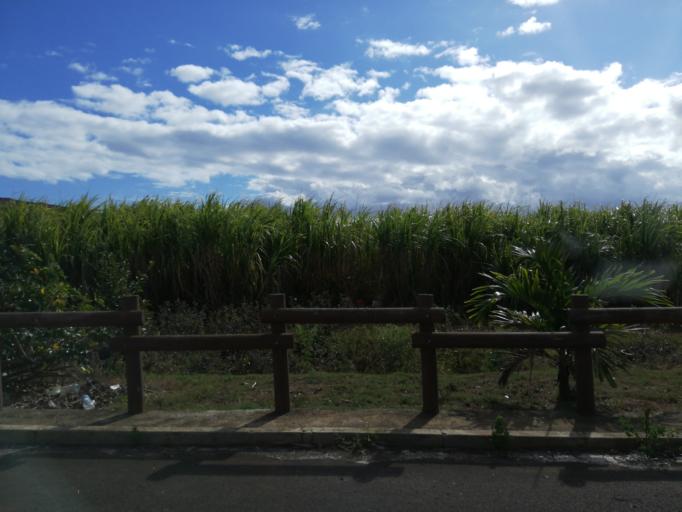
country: MU
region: Black River
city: Petite Riviere
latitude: -20.2238
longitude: 57.4546
